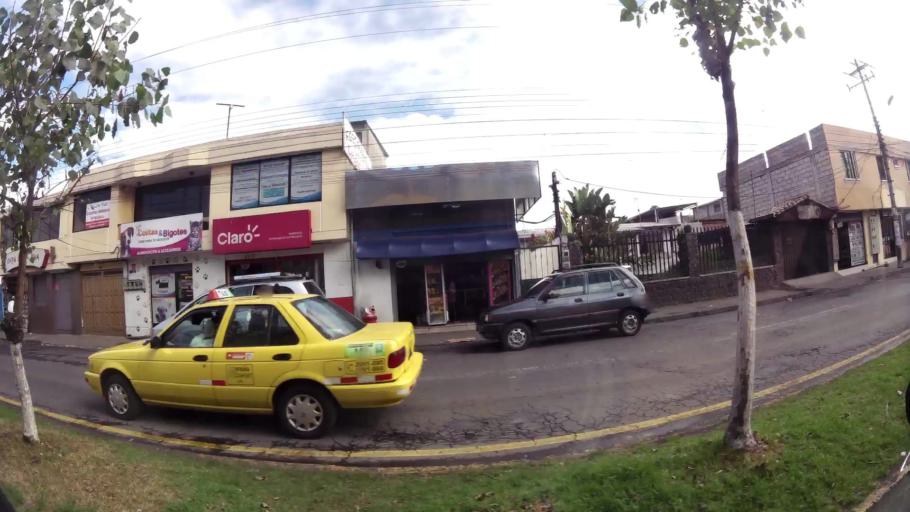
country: EC
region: Pichincha
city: Sangolqui
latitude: -0.3330
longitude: -78.4439
